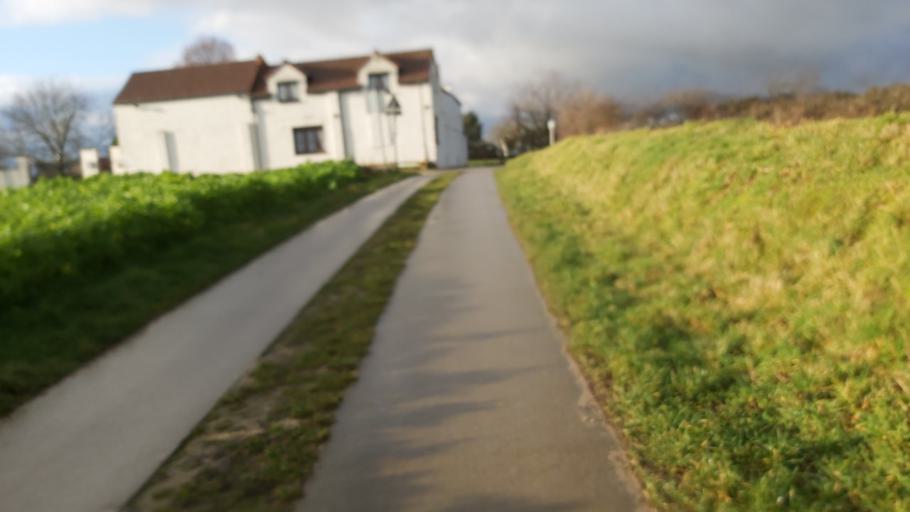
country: BE
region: Flanders
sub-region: Provincie Vlaams-Brabant
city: Tienen
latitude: 50.8226
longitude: 4.9414
